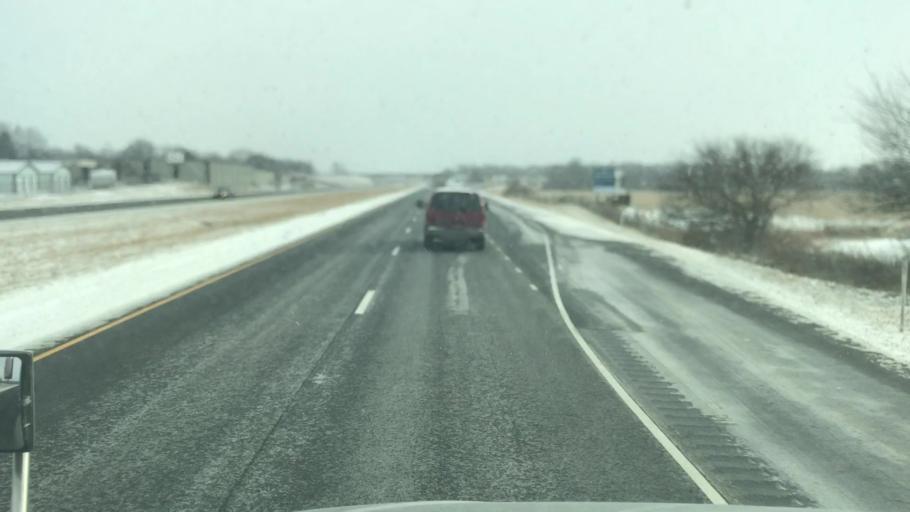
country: US
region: Indiana
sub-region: Hancock County
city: New Palestine
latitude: 39.6656
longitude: -85.9483
